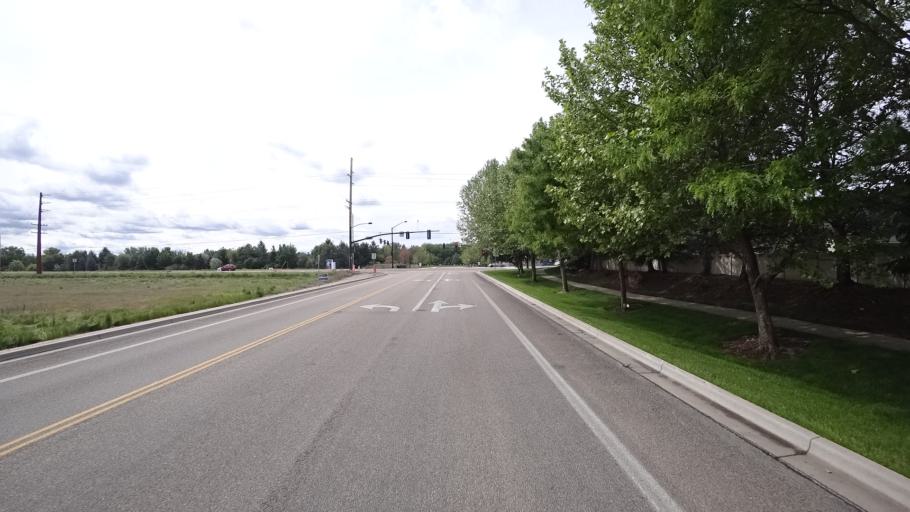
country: US
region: Idaho
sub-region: Ada County
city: Eagle
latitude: 43.6963
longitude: -116.3826
